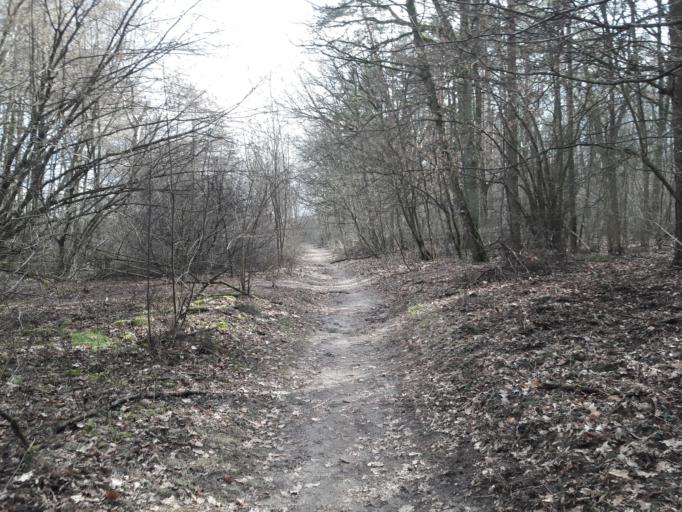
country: PL
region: Greater Poland Voivodeship
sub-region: Powiat poznanski
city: Suchy Las
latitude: 52.4785
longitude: 16.8977
